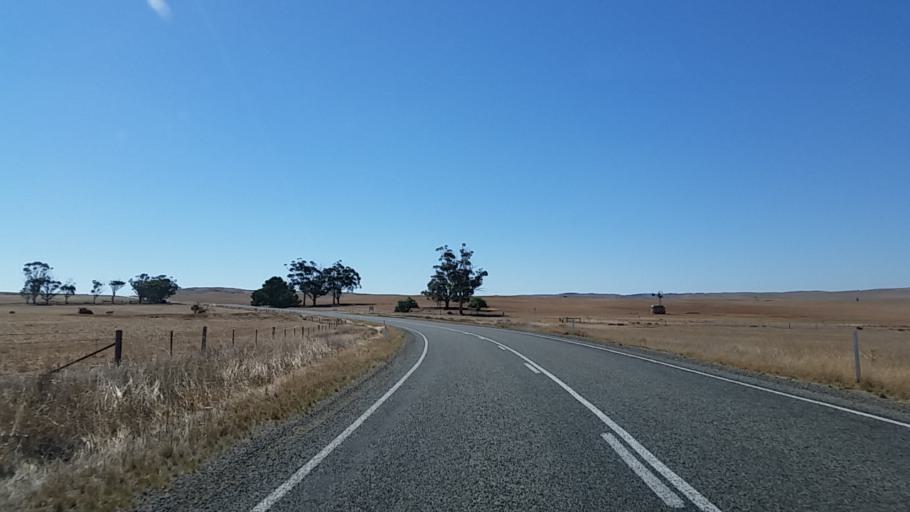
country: AU
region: South Australia
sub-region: Northern Areas
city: Jamestown
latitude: -33.3395
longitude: 138.8929
